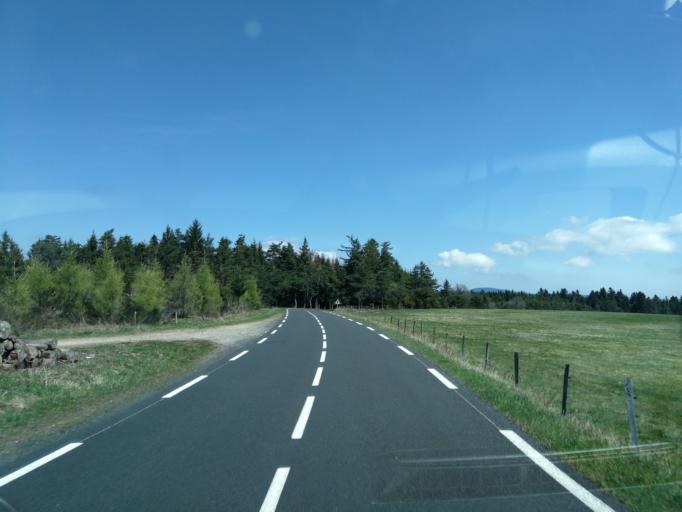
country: FR
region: Rhone-Alpes
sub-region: Departement de l'Ardeche
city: Saint-Agreve
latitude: 45.0936
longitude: 4.3969
